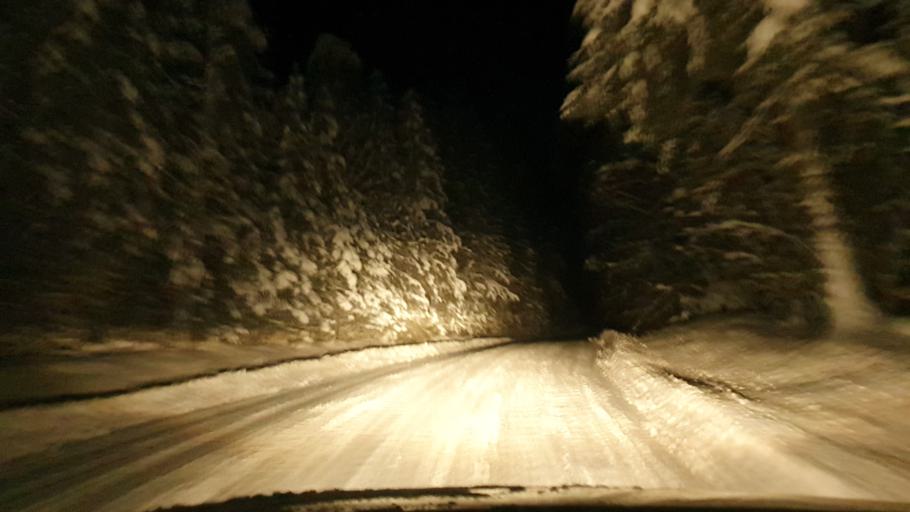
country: EE
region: Vorumaa
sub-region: Antsla vald
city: Vana-Antsla
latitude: 57.9475
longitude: 26.6254
